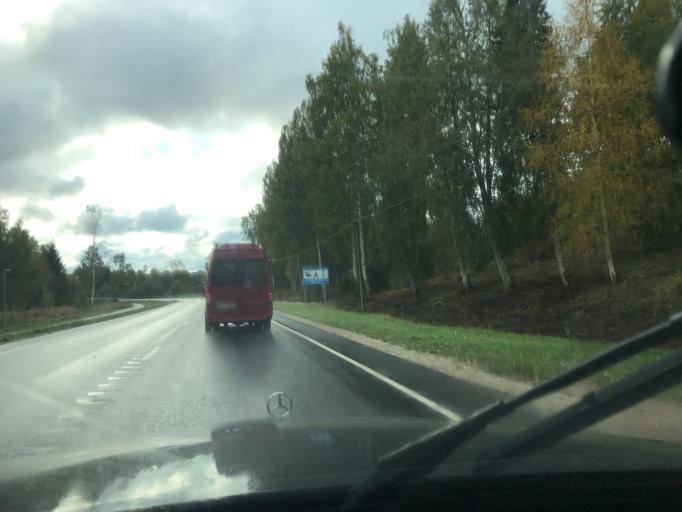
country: EE
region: Viljandimaa
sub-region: Karksi vald
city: Karksi-Nuia
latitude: 58.0146
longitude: 25.6866
